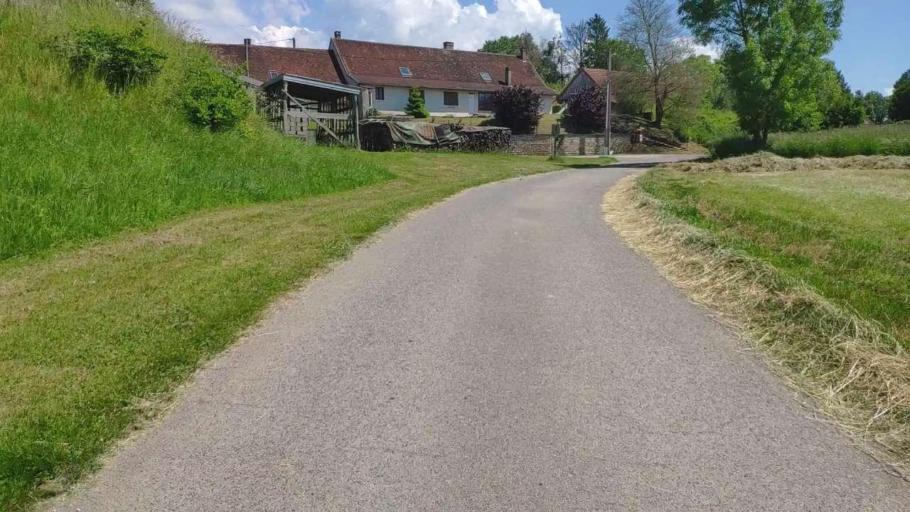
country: FR
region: Franche-Comte
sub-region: Departement du Jura
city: Bletterans
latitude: 46.7508
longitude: 5.4022
